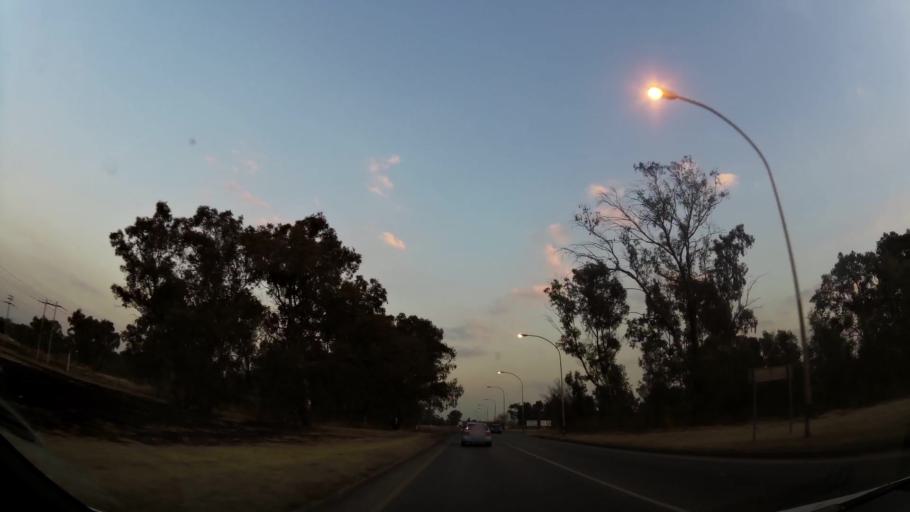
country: ZA
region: Gauteng
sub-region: Ekurhuleni Metropolitan Municipality
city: Springs
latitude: -26.2677
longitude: 28.4279
